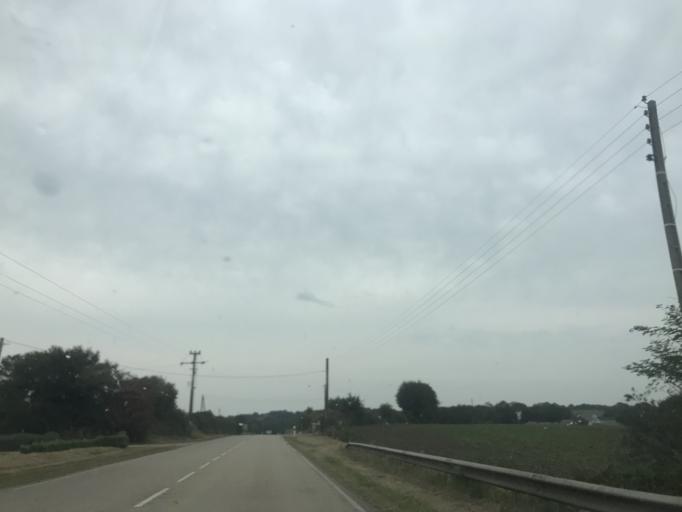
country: FR
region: Brittany
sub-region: Departement du Finistere
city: Plouneour-Menez
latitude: 48.4507
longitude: -3.8795
